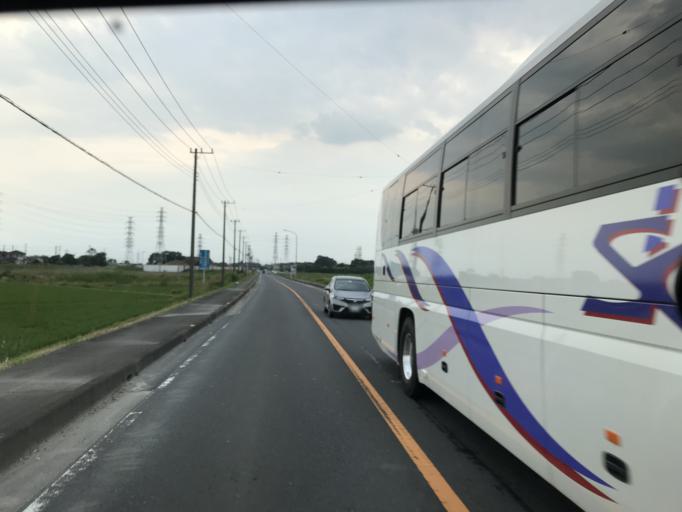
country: JP
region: Saitama
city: Shiraoka
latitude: 36.0135
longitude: 139.6846
